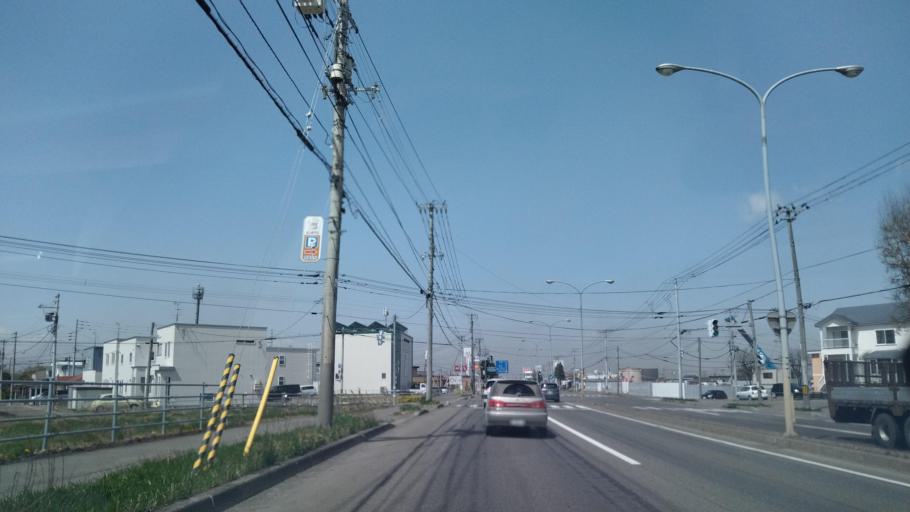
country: JP
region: Hokkaido
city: Obihiro
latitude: 42.9165
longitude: 143.2478
